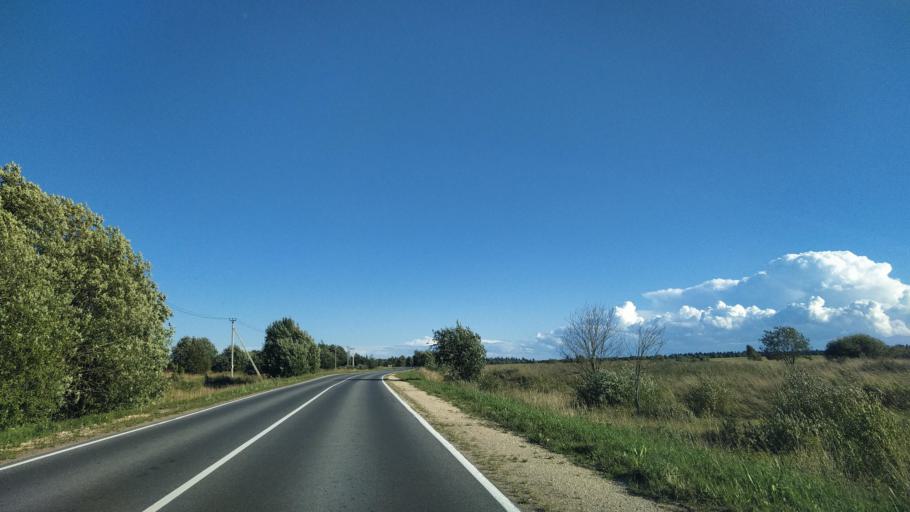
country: RU
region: Leningrad
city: Siverskiy
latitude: 59.3276
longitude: 30.0345
